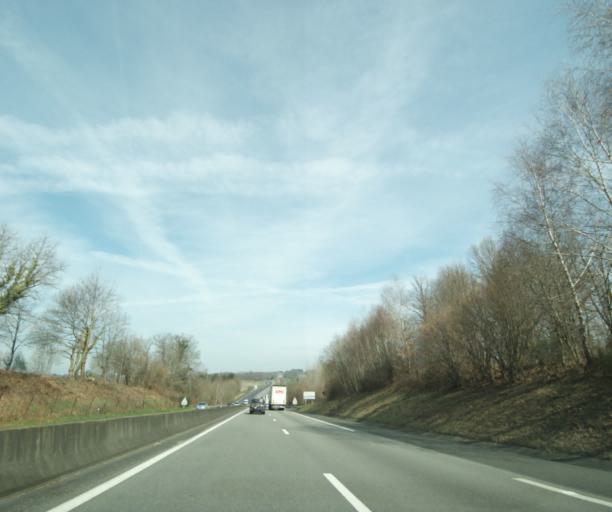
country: FR
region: Limousin
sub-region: Departement de la Correze
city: Uzerche
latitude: 45.3754
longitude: 1.5739
